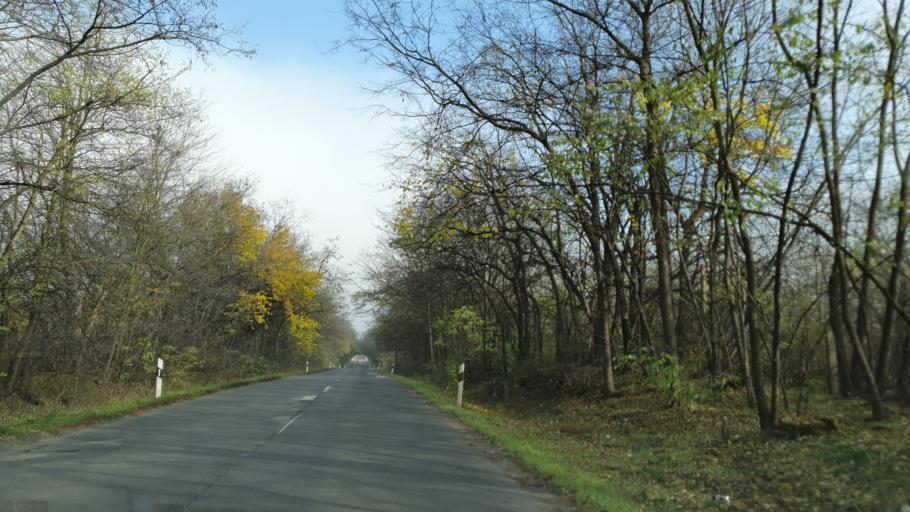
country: HU
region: Pest
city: Orbottyan
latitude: 47.6698
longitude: 19.2448
